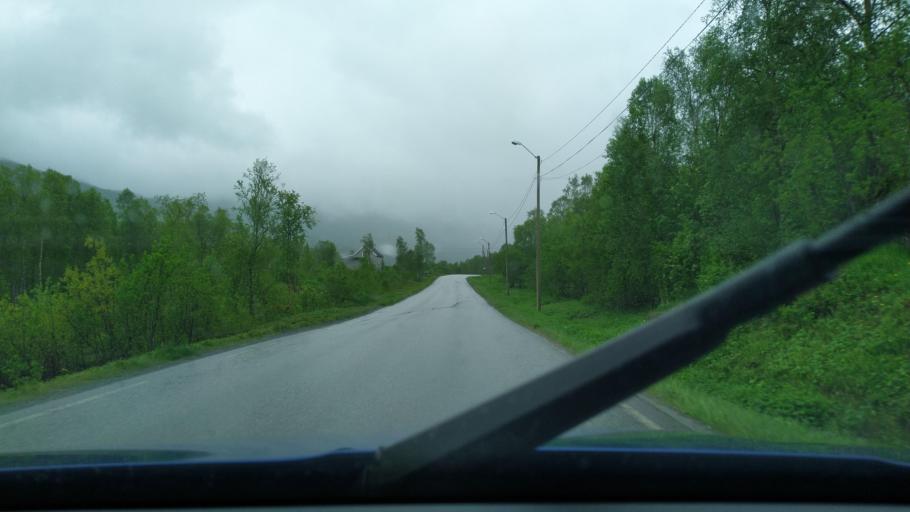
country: NO
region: Troms
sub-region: Dyroy
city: Brostadbotn
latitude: 69.0439
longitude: 17.7310
